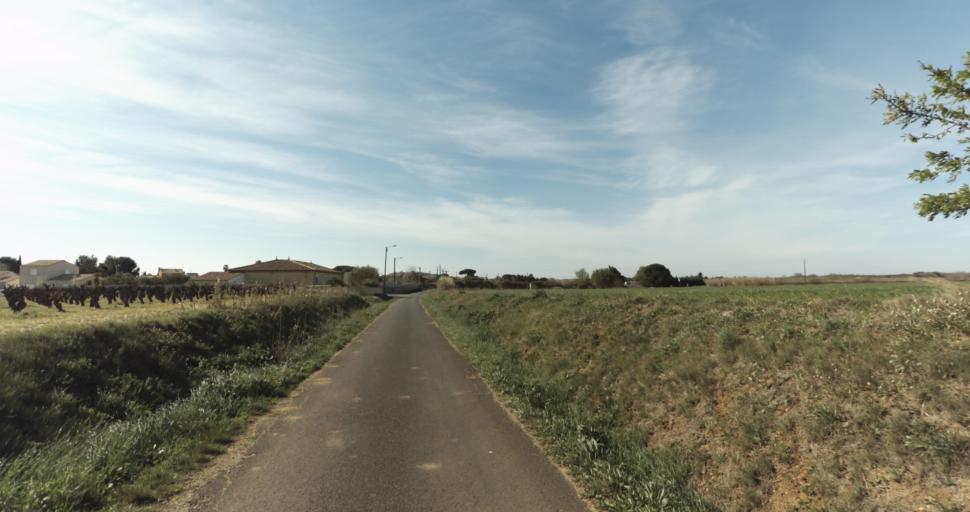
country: FR
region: Languedoc-Roussillon
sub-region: Departement de l'Herault
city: Marseillan
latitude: 43.3398
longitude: 3.5174
